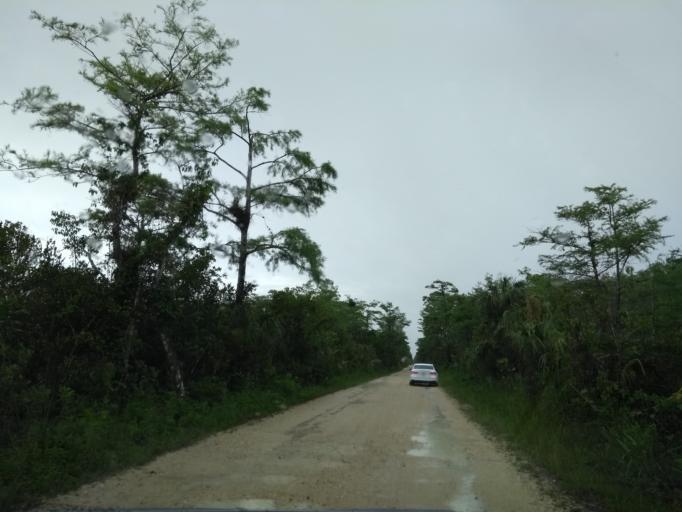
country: US
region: Florida
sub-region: Miami-Dade County
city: The Hammocks
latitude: 25.7602
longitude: -81.0374
